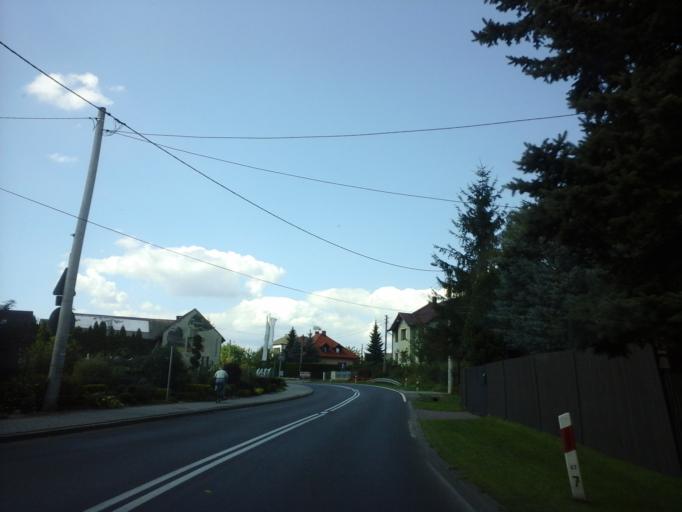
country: PL
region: Lesser Poland Voivodeship
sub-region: Powiat oswiecimski
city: Przeciszow
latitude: 50.0085
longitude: 19.3741
